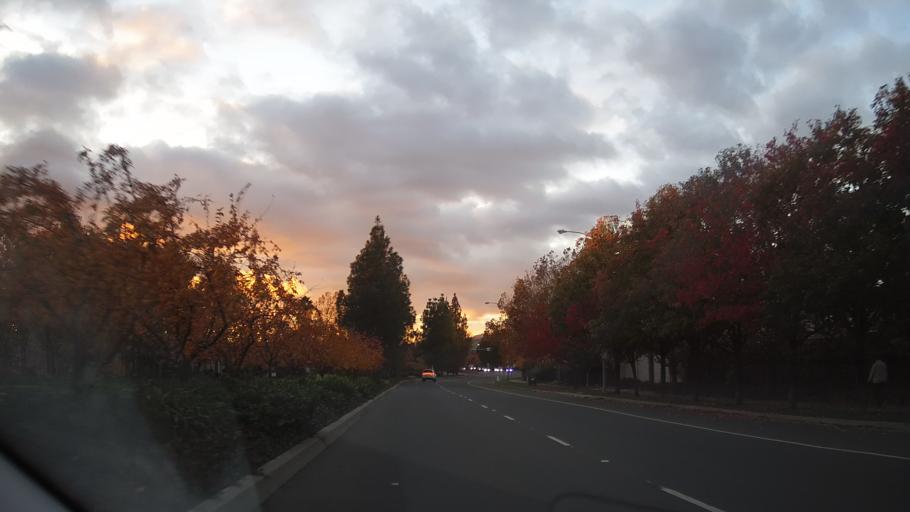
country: US
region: California
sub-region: Solano County
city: Fairfield
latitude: 38.2927
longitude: -122.0174
